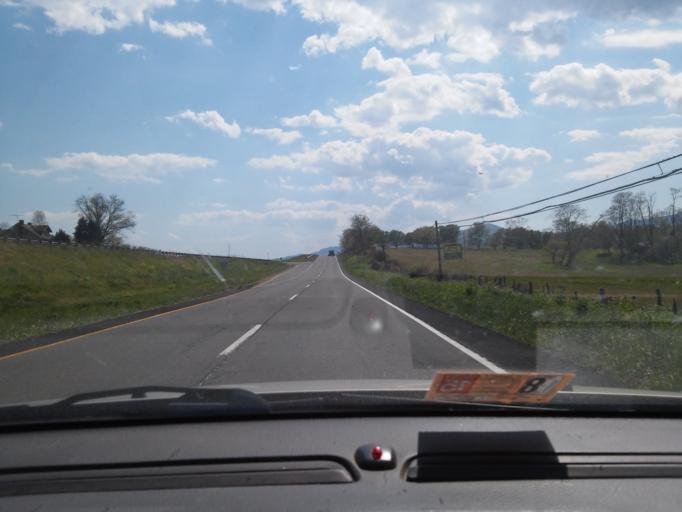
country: US
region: Virginia
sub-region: Rappahannock County
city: Washington
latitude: 38.6776
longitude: -78.2092
